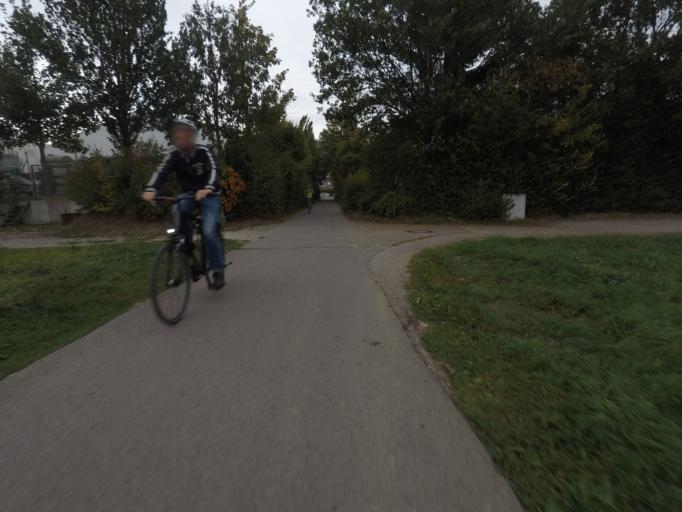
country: DE
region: Baden-Wuerttemberg
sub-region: Regierungsbezirk Stuttgart
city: Leinfelden-Echterdingen
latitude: 48.7187
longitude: 9.1293
